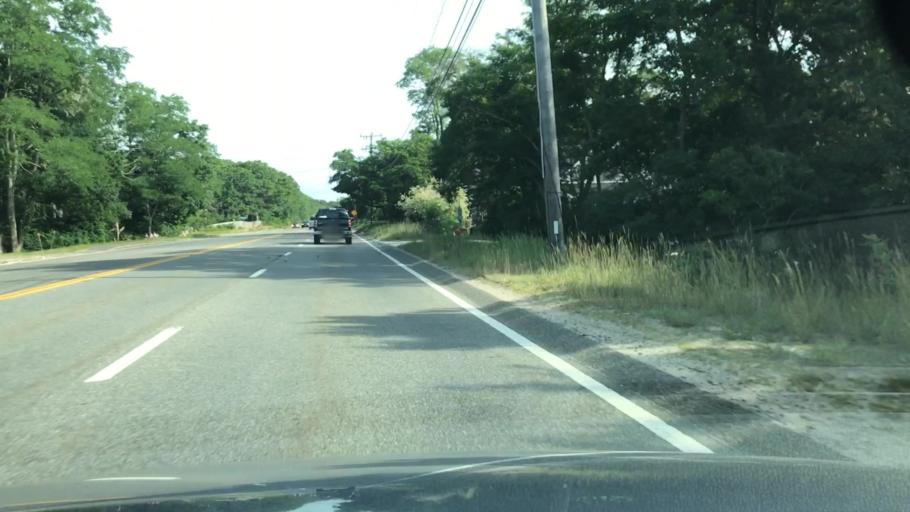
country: US
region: Massachusetts
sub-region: Barnstable County
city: North Eastham
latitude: 41.8728
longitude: -69.9864
